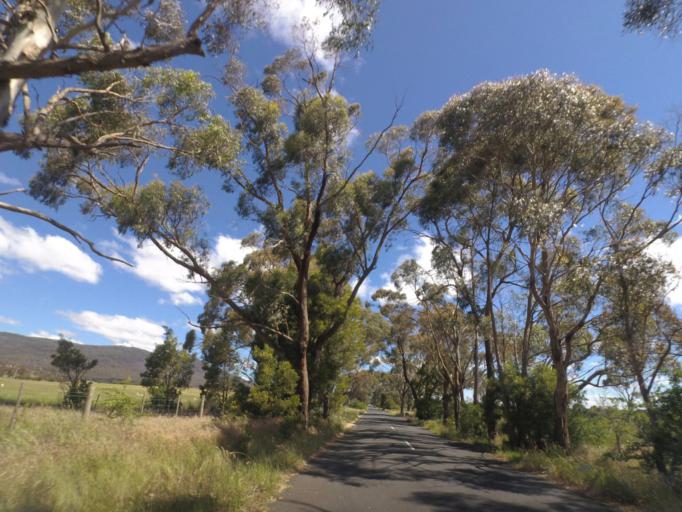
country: AU
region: Victoria
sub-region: Hume
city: Sunbury
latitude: -37.3417
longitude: 144.5570
